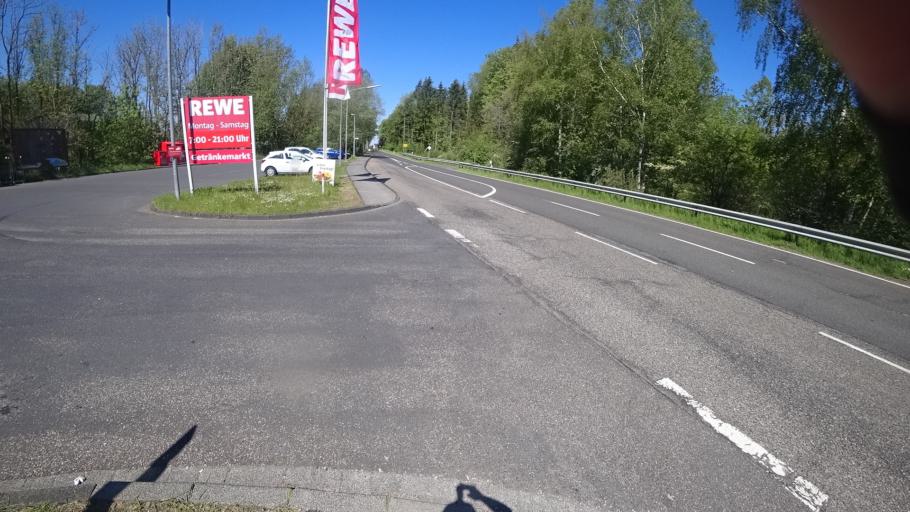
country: DE
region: Rheinland-Pfalz
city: Elkenroth
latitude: 50.7286
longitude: 7.8926
